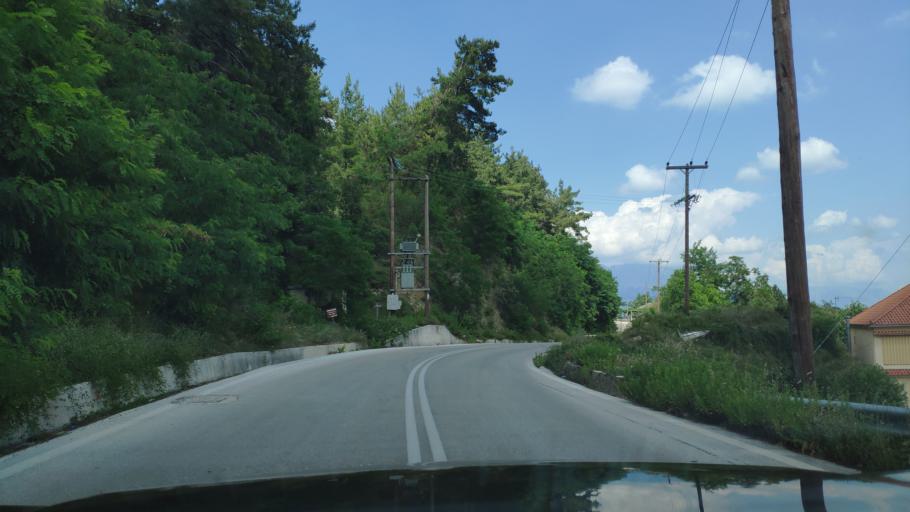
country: GR
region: Epirus
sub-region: Nomos Artas
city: Agios Dimitrios
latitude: 39.3214
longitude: 20.9926
